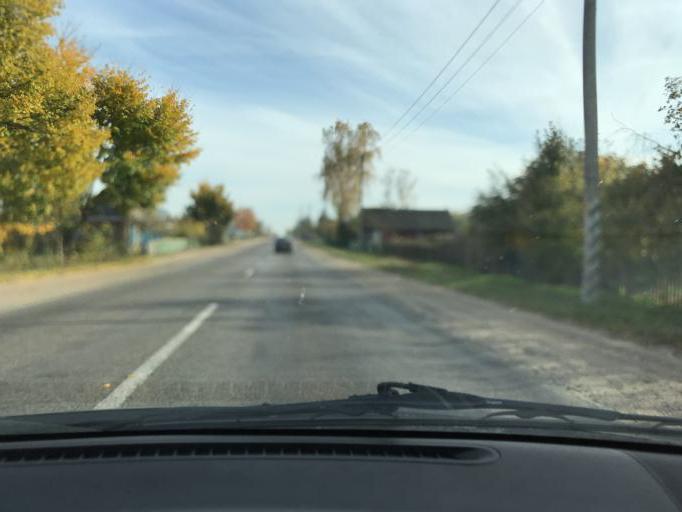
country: BY
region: Brest
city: Asnyezhytsy
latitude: 52.2267
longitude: 26.0240
